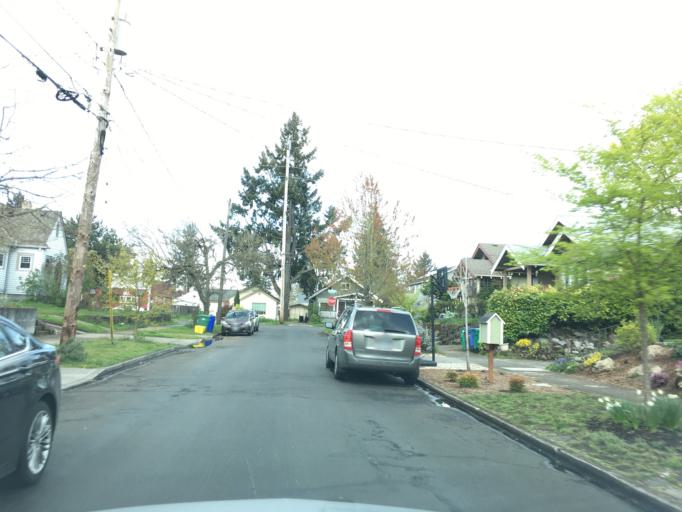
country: US
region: Oregon
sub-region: Multnomah County
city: Lents
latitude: 45.5477
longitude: -122.5993
